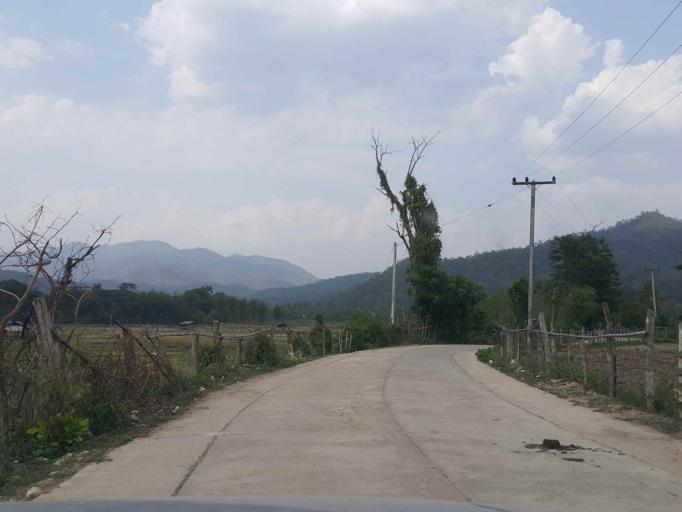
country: TH
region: Chiang Mai
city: Wiang Haeng
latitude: 19.3891
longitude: 98.7171
